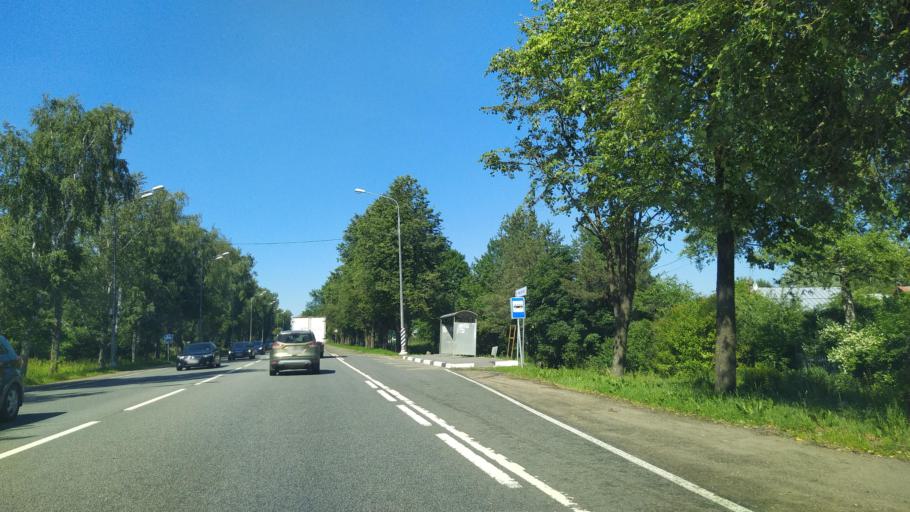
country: RU
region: Leningrad
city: Voyskovitsy
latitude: 59.4477
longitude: 29.9853
